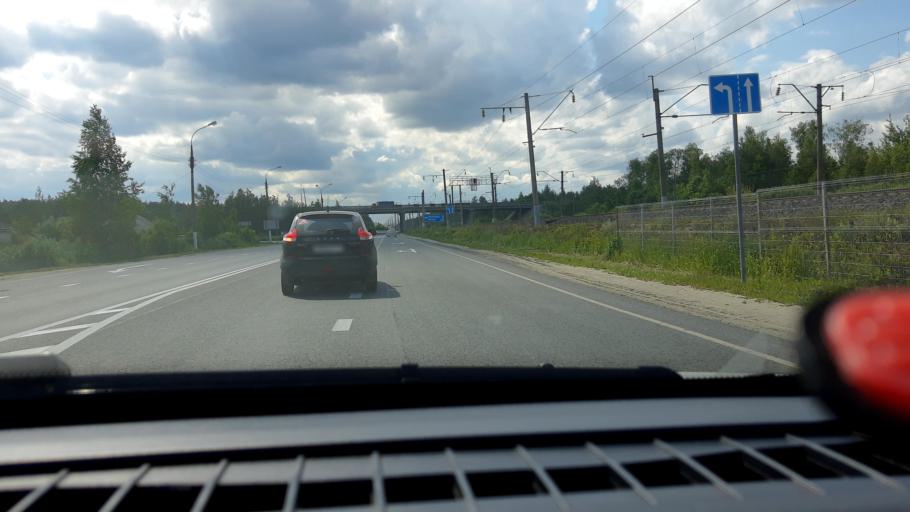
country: RU
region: Nizjnij Novgorod
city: Gorbatovka
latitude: 56.2617
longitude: 43.7129
